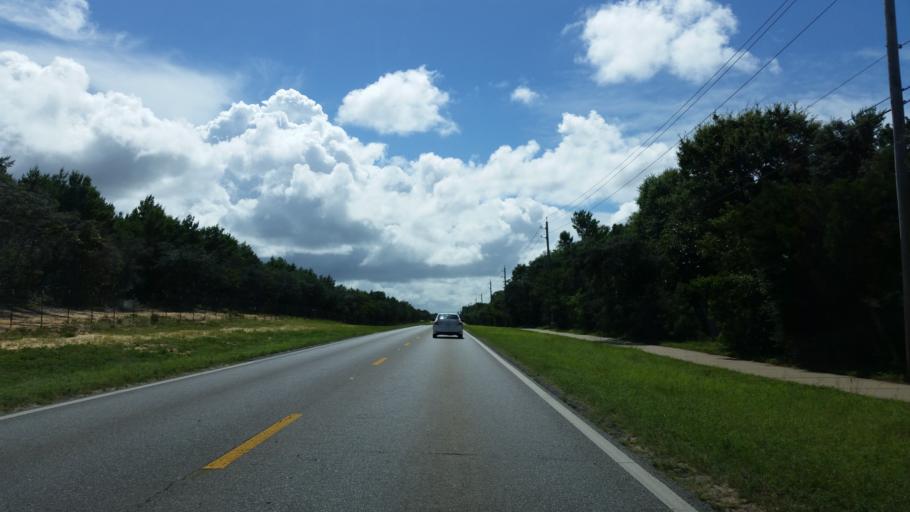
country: US
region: Florida
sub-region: Santa Rosa County
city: Holley
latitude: 30.4326
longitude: -86.8855
